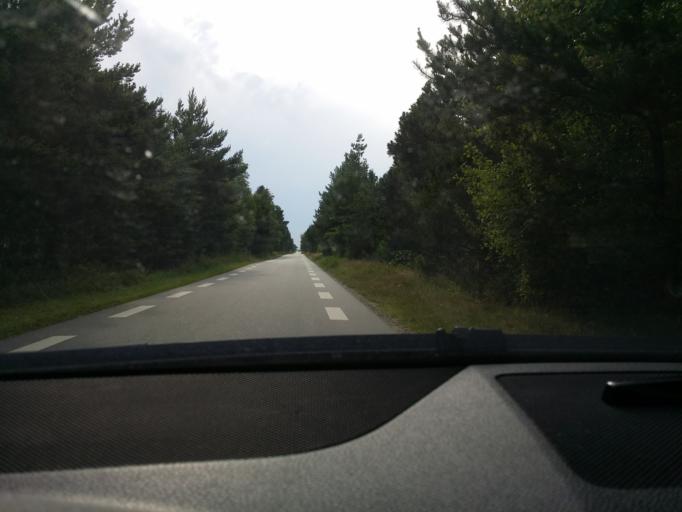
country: DE
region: Schleswig-Holstein
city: List
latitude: 55.1290
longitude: 8.5372
